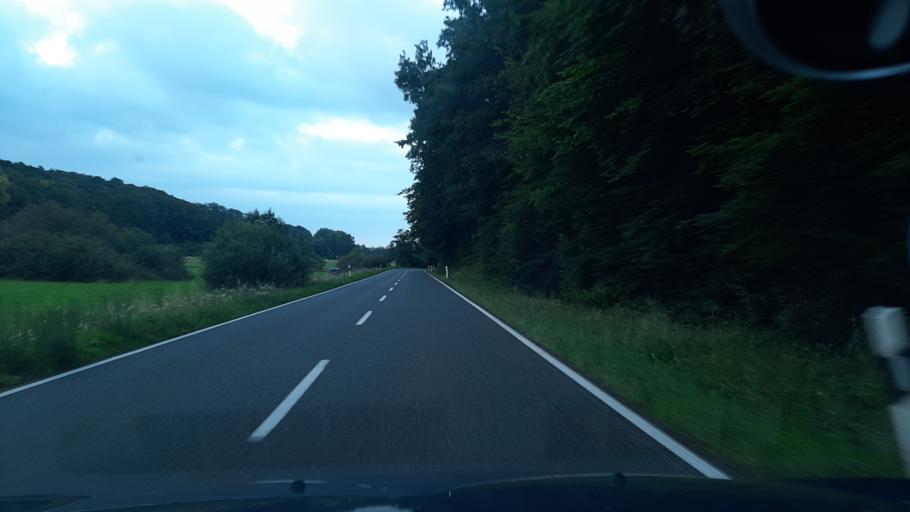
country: DE
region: North Rhine-Westphalia
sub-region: Regierungsbezirk Koln
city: Mechernich
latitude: 50.6097
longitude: 6.6954
